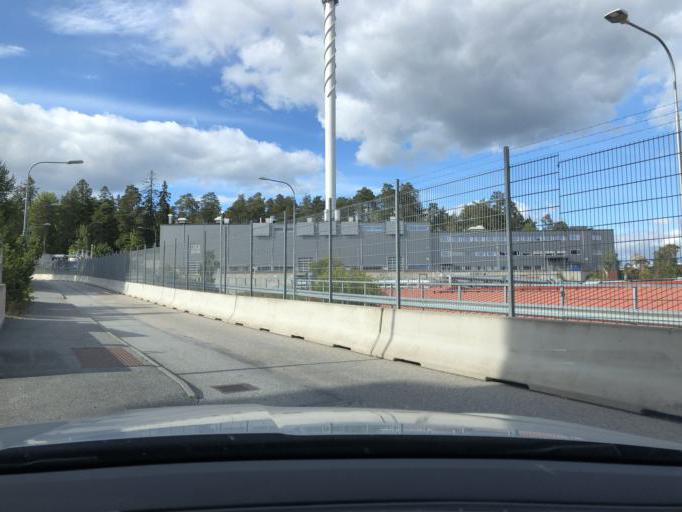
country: SE
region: Stockholm
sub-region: Sodertalje Kommun
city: Soedertaelje
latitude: 59.2048
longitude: 17.6130
